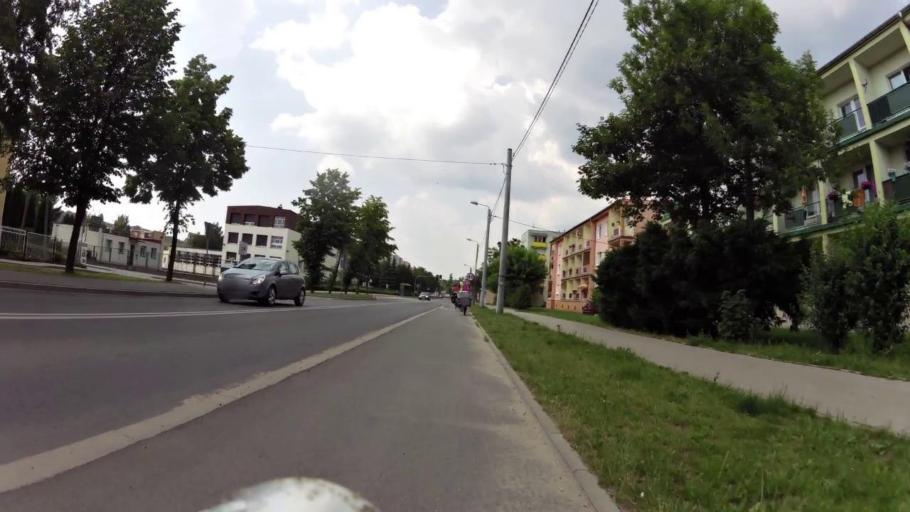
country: PL
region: Kujawsko-Pomorskie
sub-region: Powiat bydgoski
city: Koronowo
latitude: 53.3072
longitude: 17.9439
